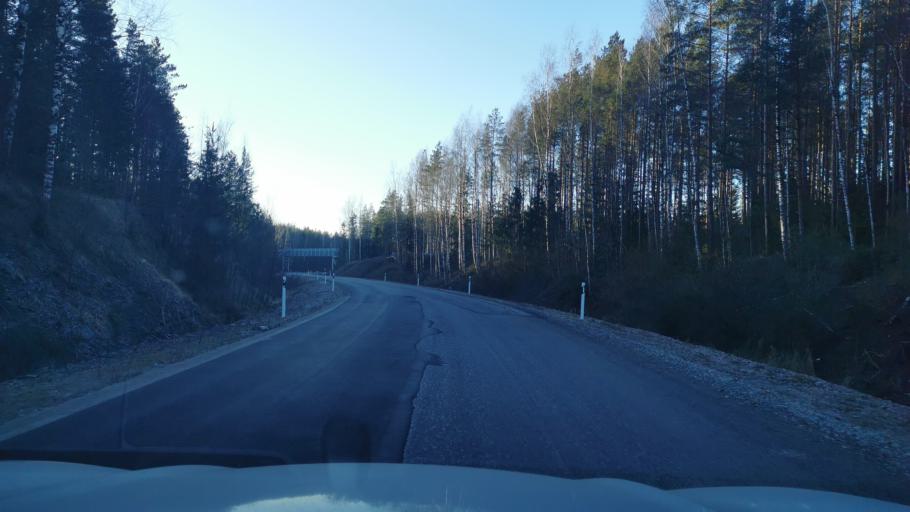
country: EE
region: Ida-Virumaa
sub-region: Kohtla-Nomme vald
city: Kohtla-Nomme
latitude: 59.3466
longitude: 27.1522
